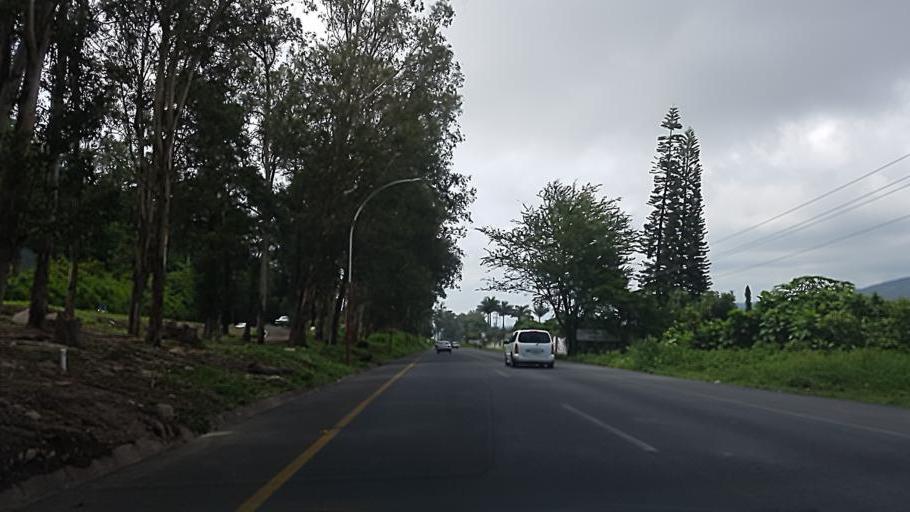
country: MX
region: Nayarit
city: Tepic
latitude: 21.5085
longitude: -104.9222
